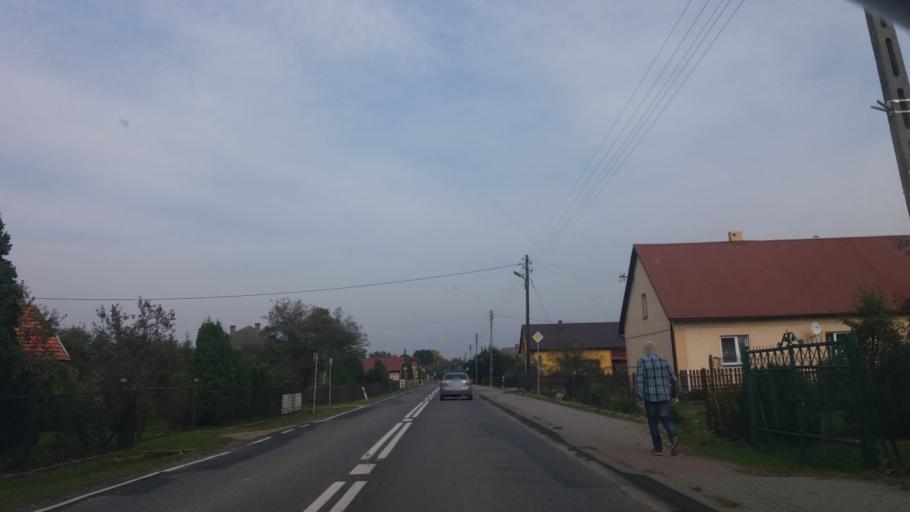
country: PL
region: Lesser Poland Voivodeship
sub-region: Powiat oswiecimski
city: Zator
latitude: 50.0193
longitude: 19.4338
